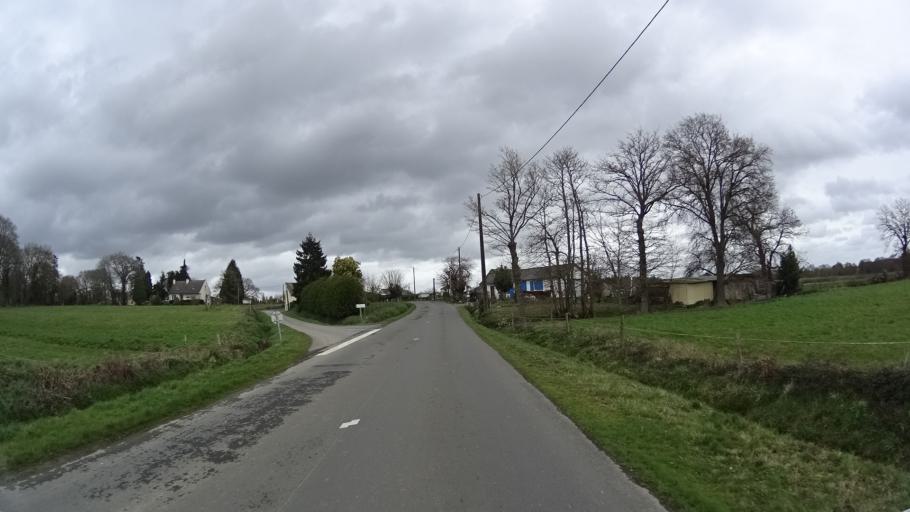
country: FR
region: Brittany
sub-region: Departement d'Ille-et-Vilaine
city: Saint-Gilles
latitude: 48.1628
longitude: -1.8312
